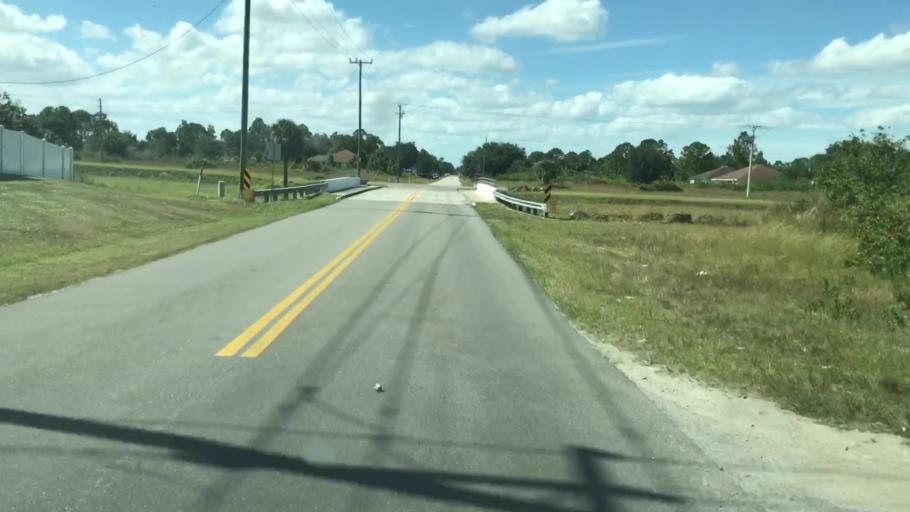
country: US
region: Florida
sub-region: Lee County
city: Lehigh Acres
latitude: 26.6610
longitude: -81.6623
